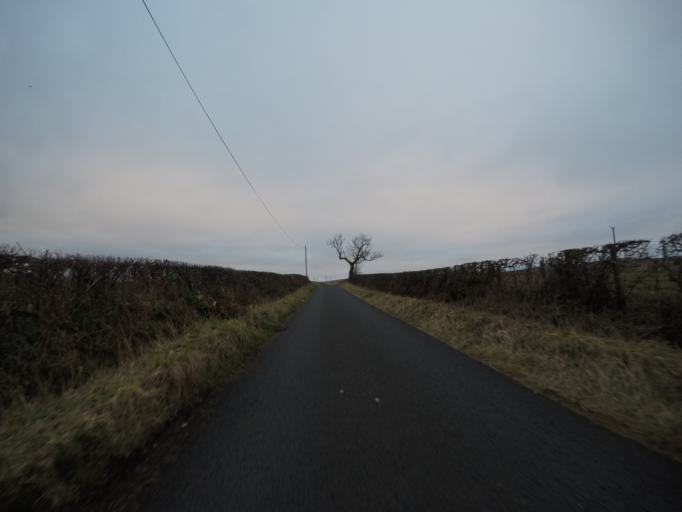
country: GB
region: Scotland
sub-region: North Ayrshire
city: Dalry
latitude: 55.7018
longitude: -4.7647
